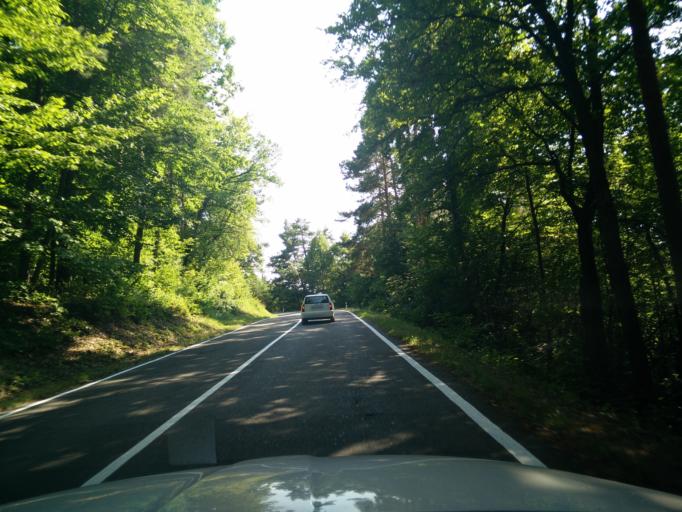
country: SK
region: Nitriansky
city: Bojnice
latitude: 48.7852
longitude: 18.5577
